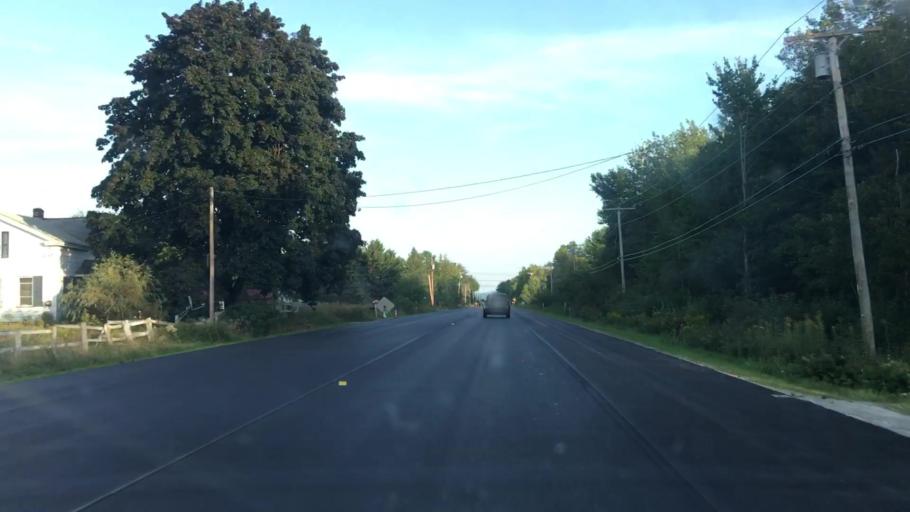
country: US
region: Maine
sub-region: Penobscot County
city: Hampden
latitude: 44.7599
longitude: -68.8466
